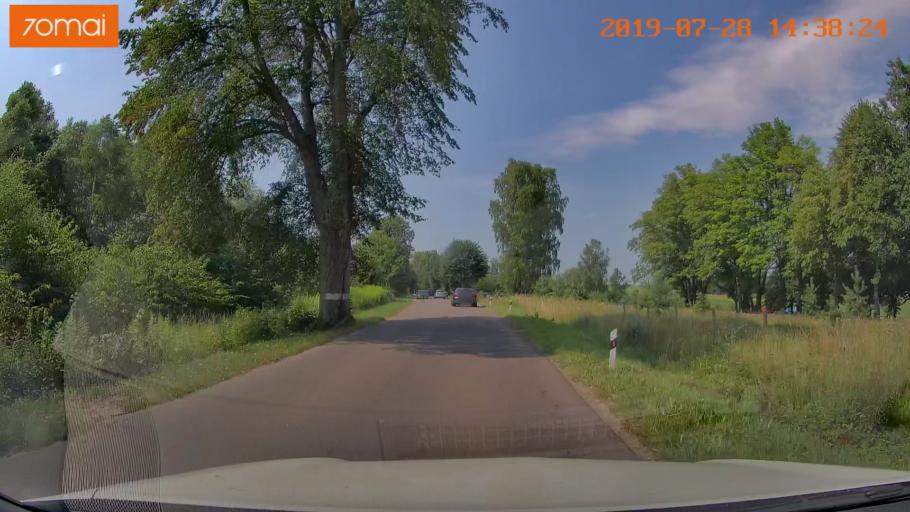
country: RU
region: Kaliningrad
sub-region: Gorod Kaliningrad
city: Yantarnyy
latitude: 54.8446
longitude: 19.9845
